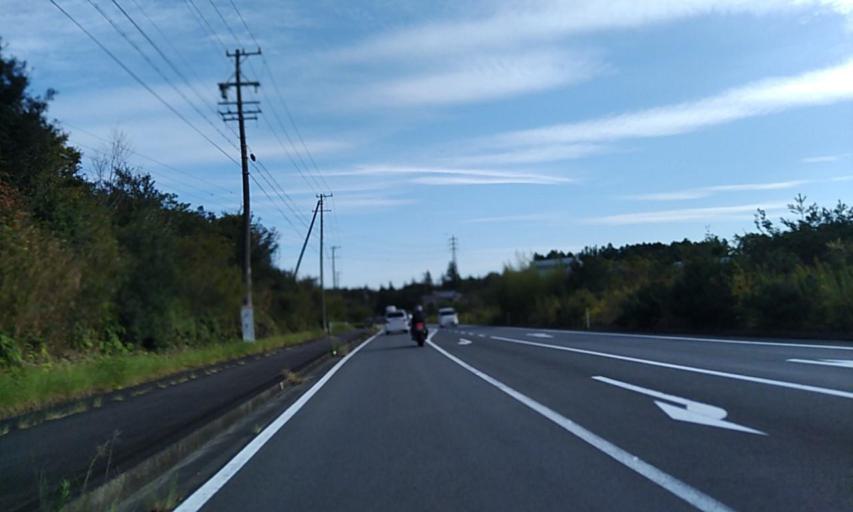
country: JP
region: Mie
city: Toba
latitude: 34.3541
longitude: 136.8075
